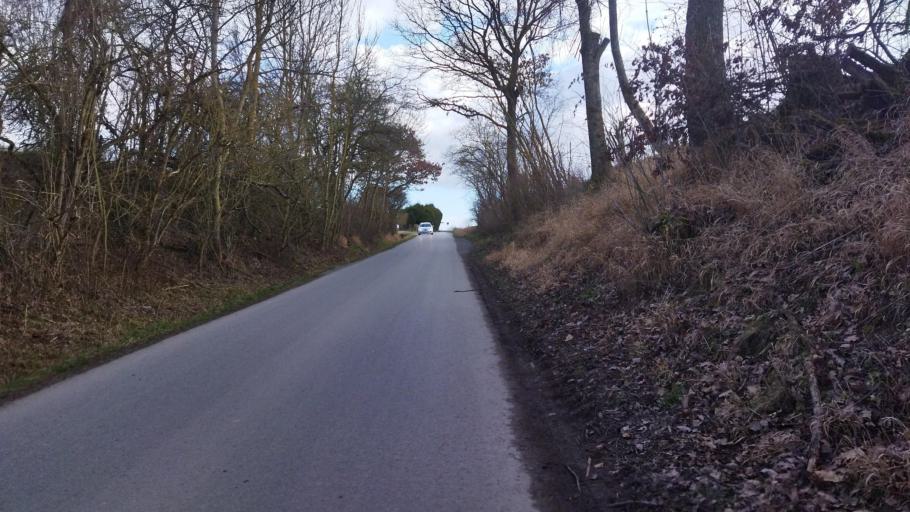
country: DE
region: Baden-Wuerttemberg
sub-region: Regierungsbezirk Stuttgart
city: Freudental
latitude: 48.9862
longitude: 9.0615
